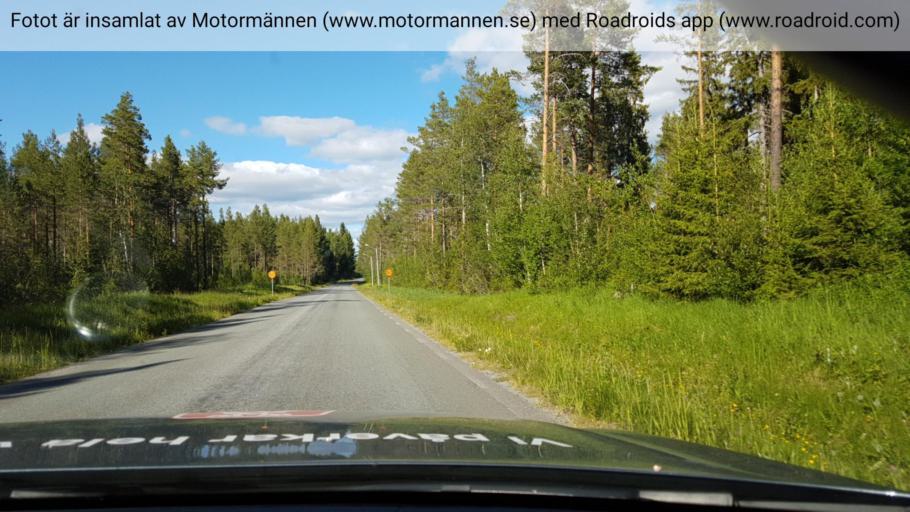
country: SE
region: Jaemtland
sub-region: Krokoms Kommun
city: Valla
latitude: 63.2995
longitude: 13.8212
